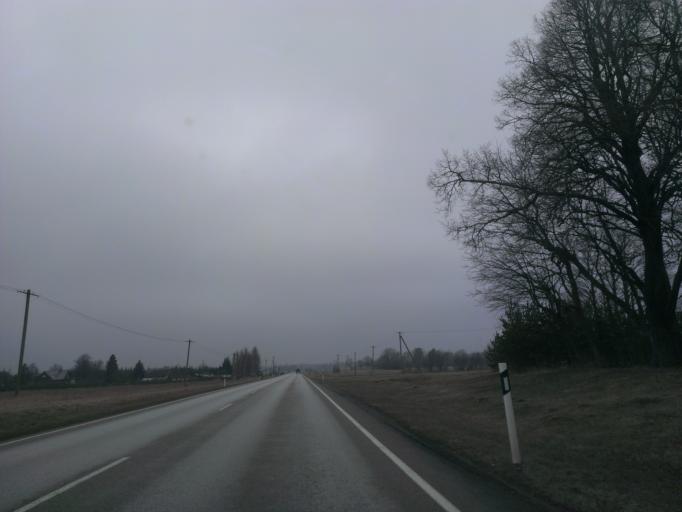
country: EE
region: Paernumaa
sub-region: Audru vald
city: Audru
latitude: 58.4613
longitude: 24.2184
